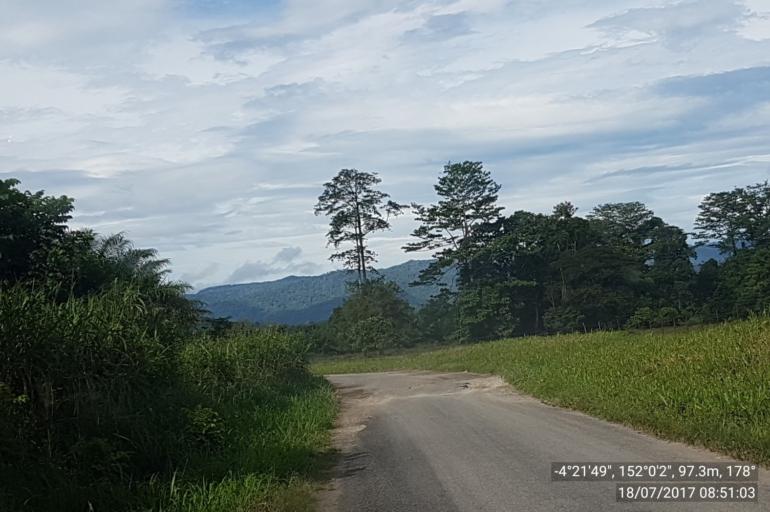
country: PG
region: East New Britain
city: Rabaul
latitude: -4.3639
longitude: 152.0008
